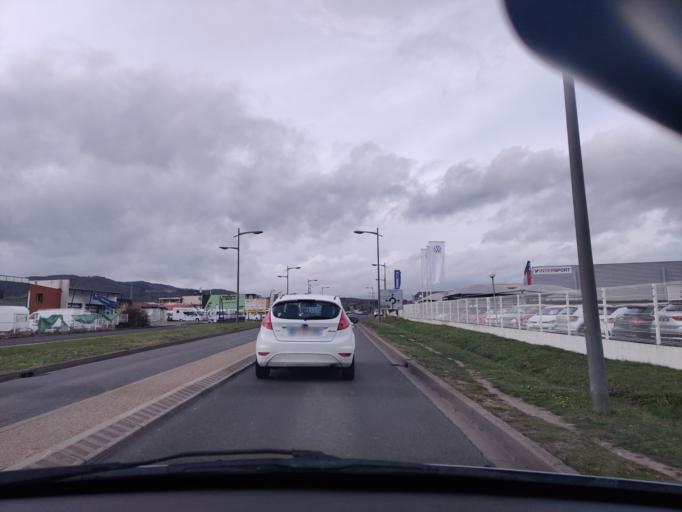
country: FR
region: Auvergne
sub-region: Departement du Puy-de-Dome
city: Marsat
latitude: 45.8877
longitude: 3.0765
